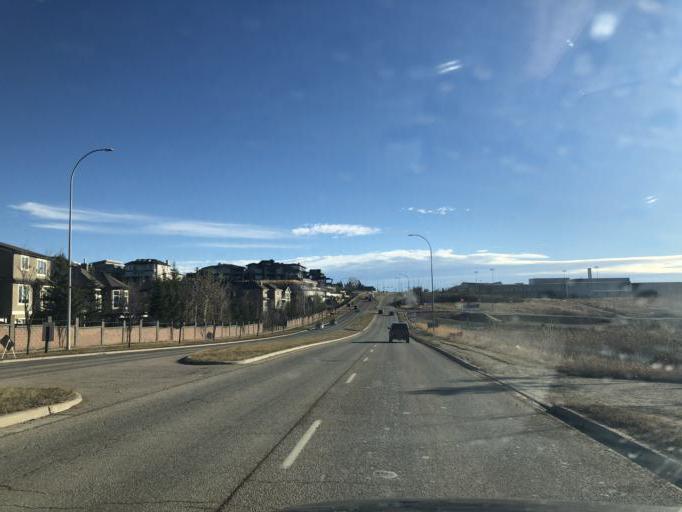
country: CA
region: Alberta
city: Calgary
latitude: 51.0379
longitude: -114.2033
